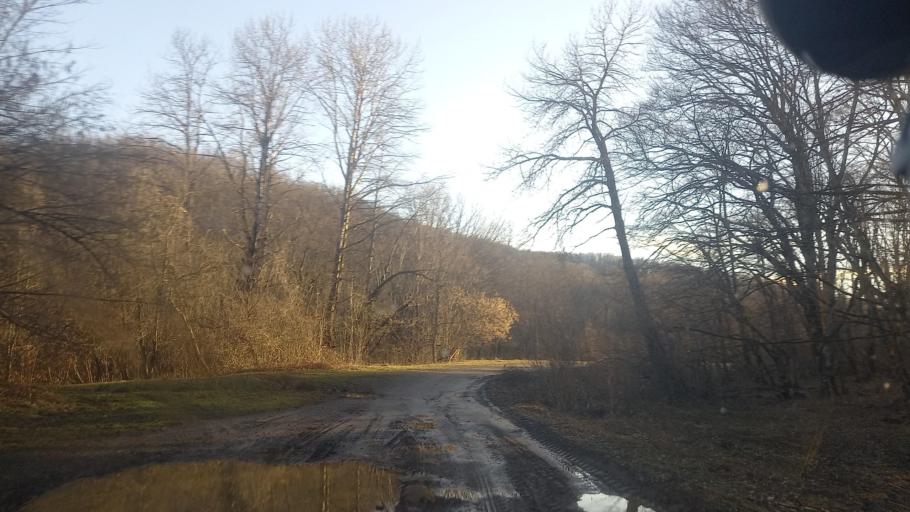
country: RU
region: Krasnodarskiy
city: Smolenskaya
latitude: 44.6127
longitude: 38.7427
